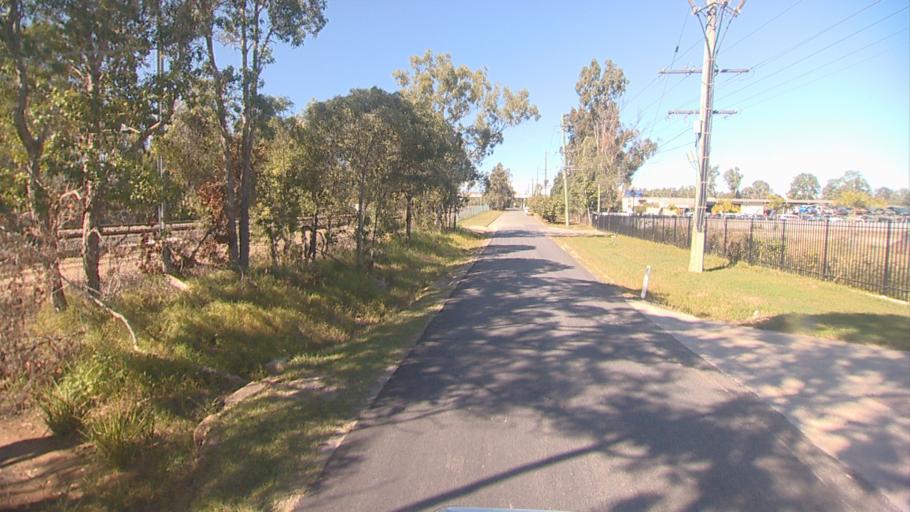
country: AU
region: Queensland
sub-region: Logan
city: Slacks Creek
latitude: -27.6646
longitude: 153.1288
